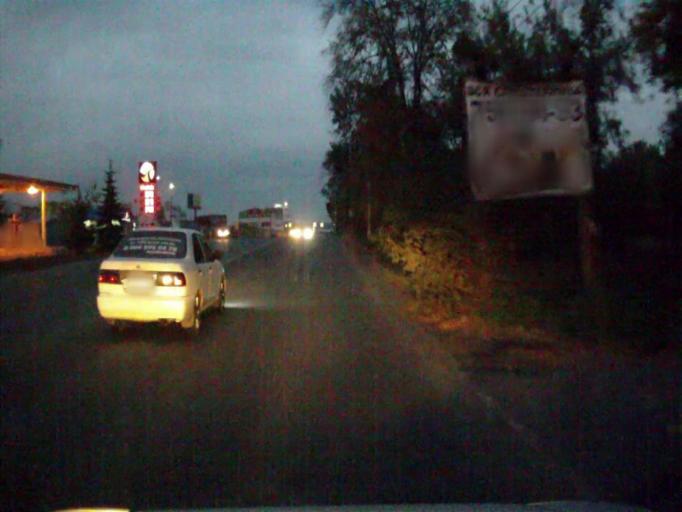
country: RU
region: Chelyabinsk
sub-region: Gorod Chelyabinsk
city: Chelyabinsk
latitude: 55.1508
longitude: 61.3034
